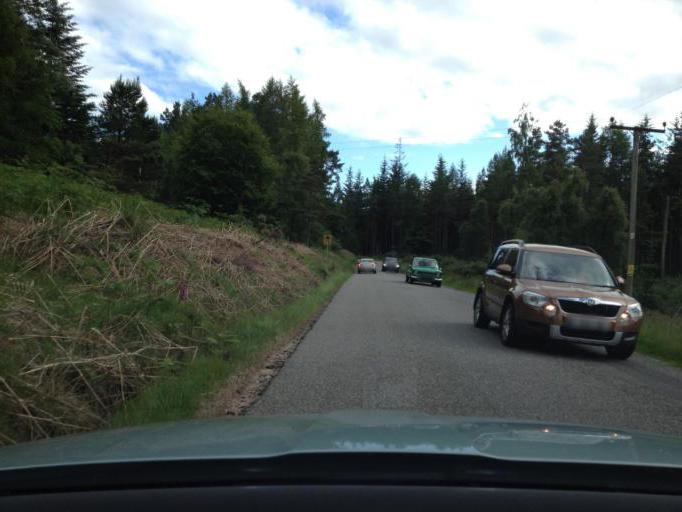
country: GB
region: Scotland
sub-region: Aberdeenshire
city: Banchory
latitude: 56.9850
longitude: -2.5753
